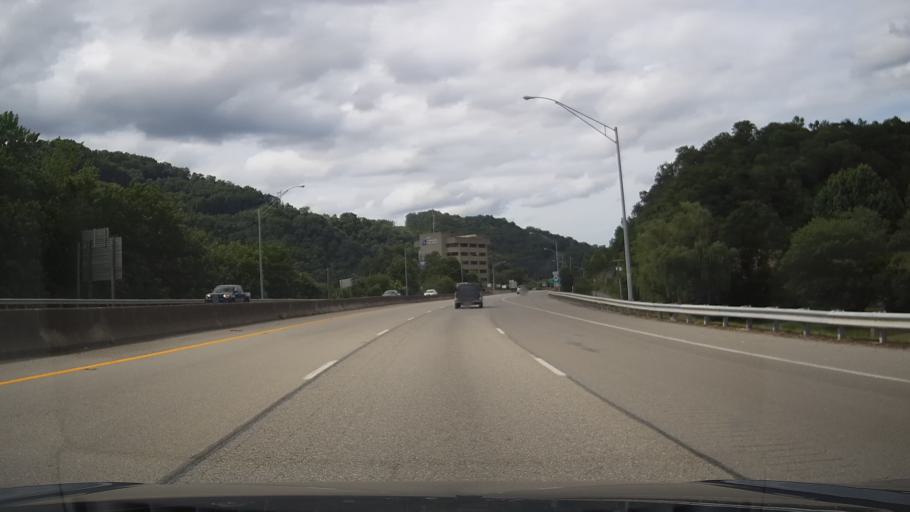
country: US
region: Kentucky
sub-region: Pike County
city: Pikeville
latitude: 37.4824
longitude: -82.5431
